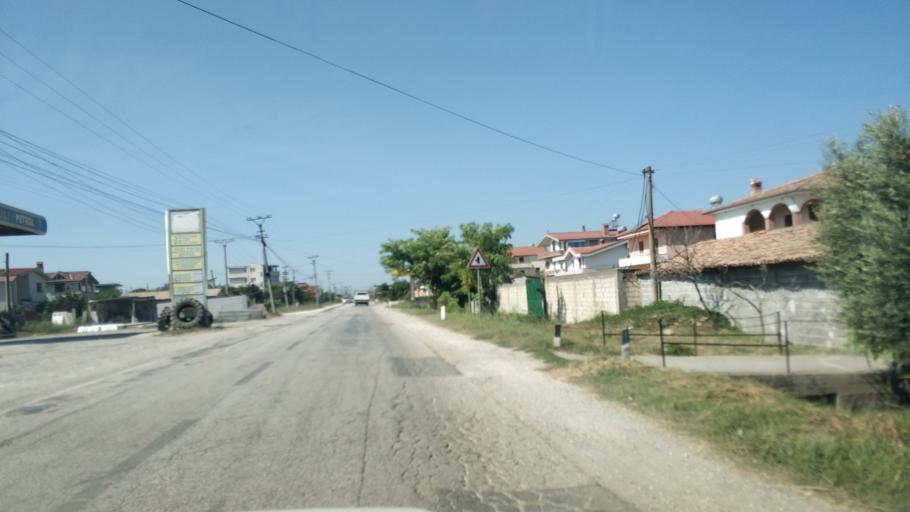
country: AL
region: Fier
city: Terbuf
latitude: 41.0519
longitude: 19.6422
